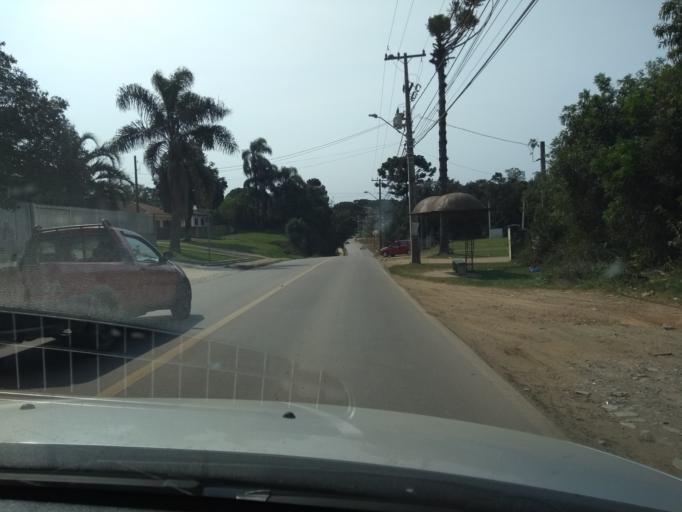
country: BR
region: Parana
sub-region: Araucaria
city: Araucaria
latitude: -25.6135
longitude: -49.3412
